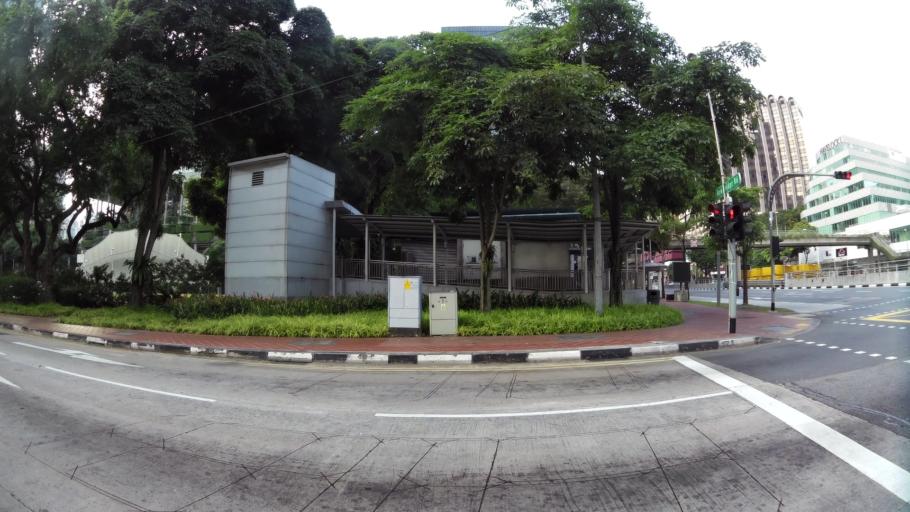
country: SG
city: Singapore
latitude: 1.2872
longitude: 103.8461
